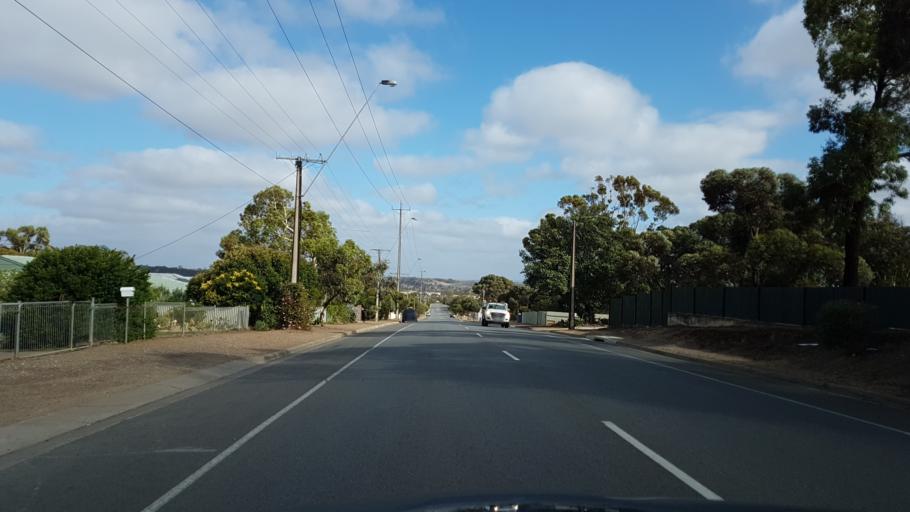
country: AU
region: South Australia
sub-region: Murray Bridge
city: Murray Bridge
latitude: -35.1208
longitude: 139.2519
